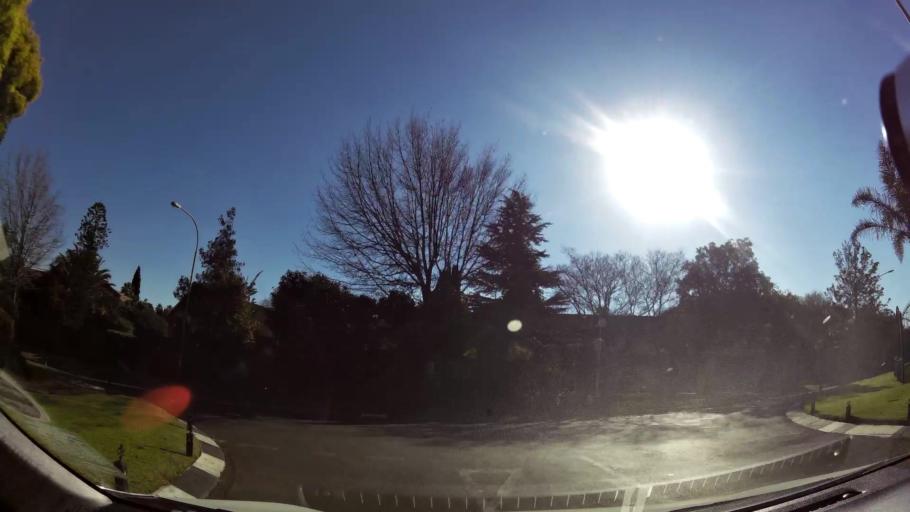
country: ZA
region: Gauteng
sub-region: City of Johannesburg Metropolitan Municipality
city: Johannesburg
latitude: -26.2804
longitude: 28.0501
